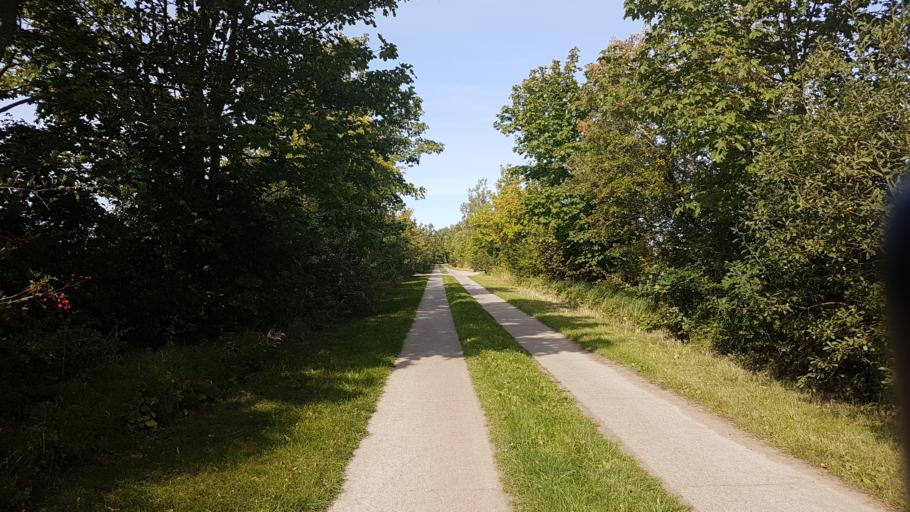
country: DE
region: Mecklenburg-Vorpommern
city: Gingst
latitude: 54.4133
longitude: 13.2575
